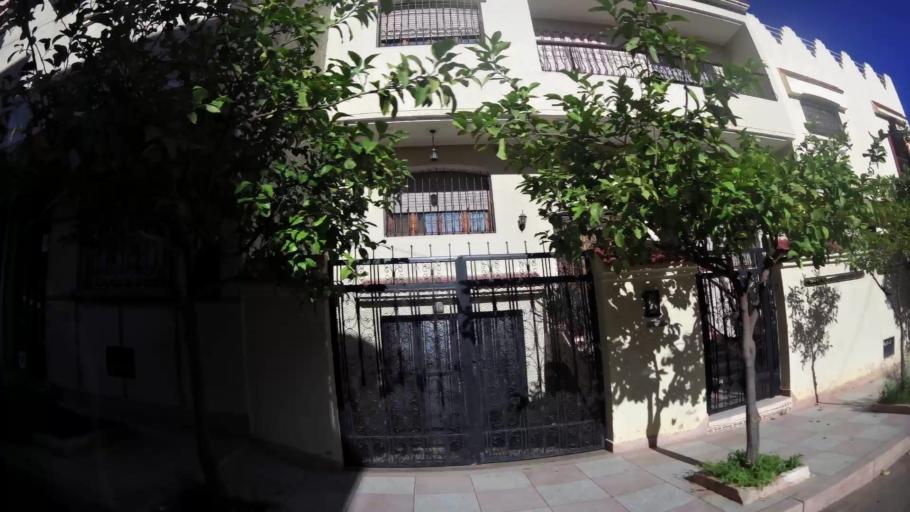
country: MA
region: Oriental
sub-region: Oujda-Angad
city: Oujda
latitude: 34.6614
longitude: -1.9026
